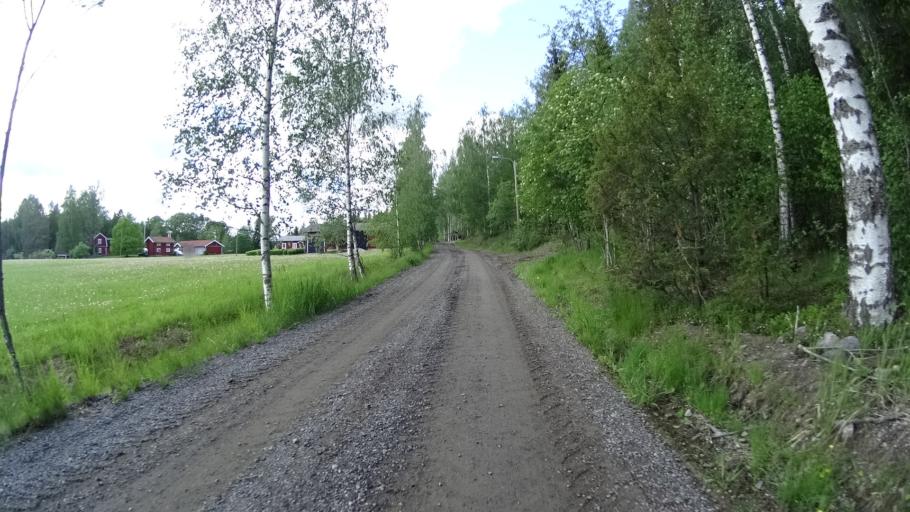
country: FI
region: Uusimaa
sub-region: Raaseporin
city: Karis
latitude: 60.1570
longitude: 23.6142
